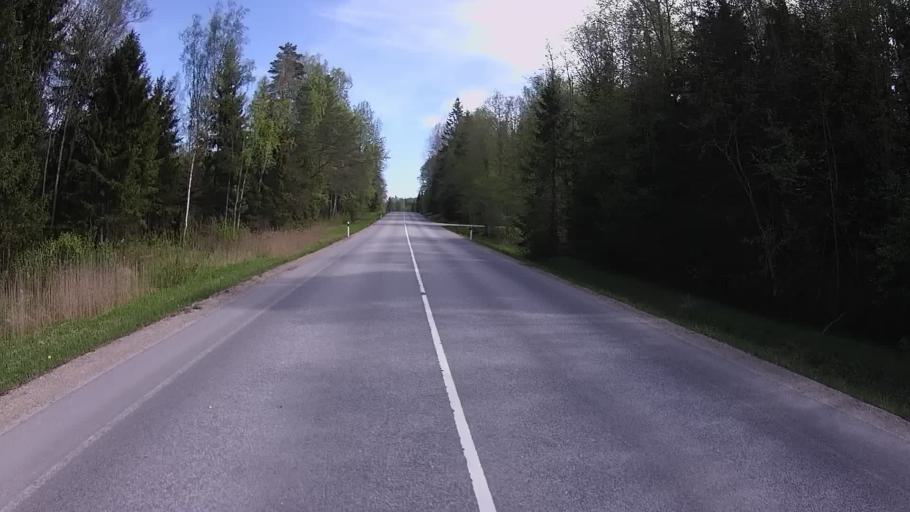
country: EE
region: Valgamaa
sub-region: Valga linn
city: Valga
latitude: 57.7143
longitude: 26.2091
